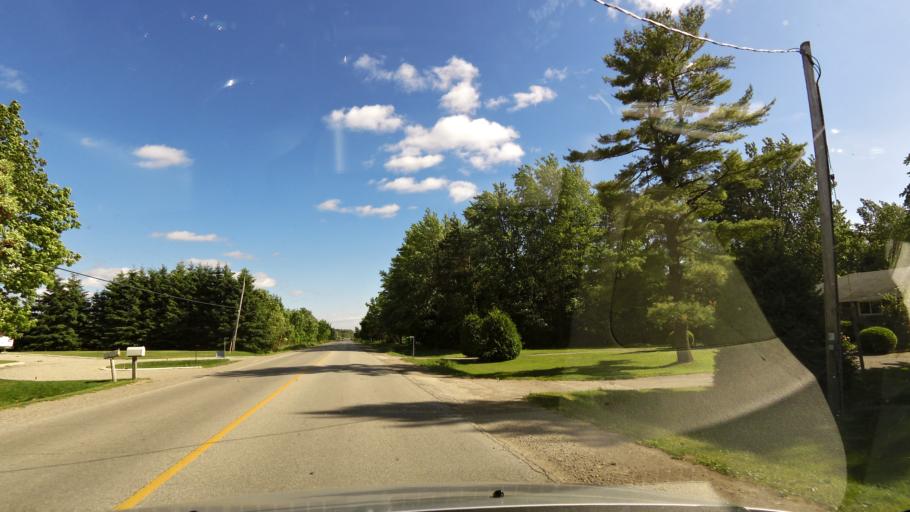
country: CA
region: Ontario
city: Bradford West Gwillimbury
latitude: 44.1482
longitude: -79.6124
